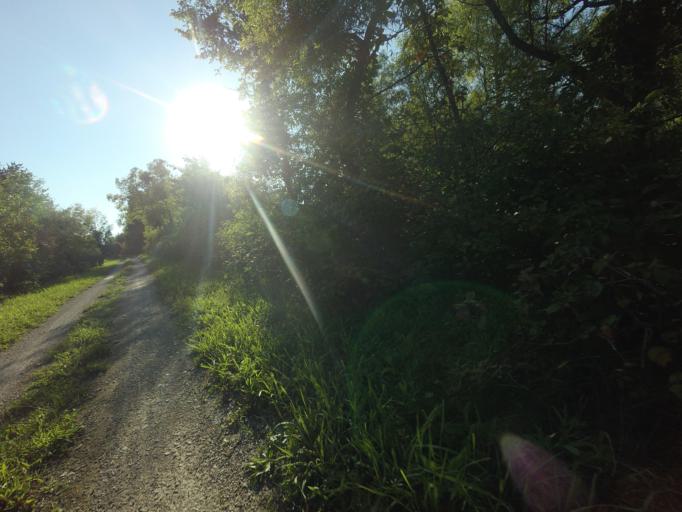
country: CA
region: Ontario
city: Goderich
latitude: 43.7511
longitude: -81.6268
